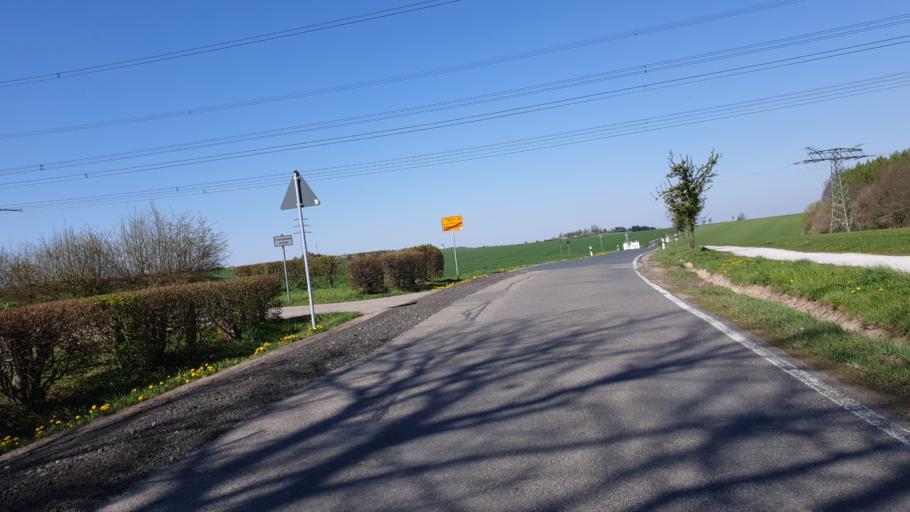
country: DE
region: Saxony
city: Taura
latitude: 50.9102
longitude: 12.8611
